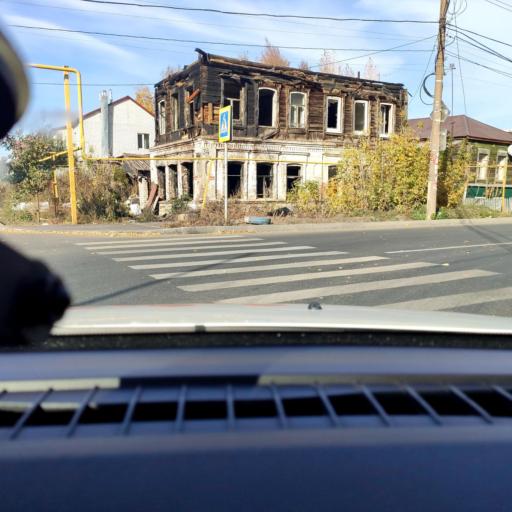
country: RU
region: Samara
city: Samara
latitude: 53.1807
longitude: 50.1343
